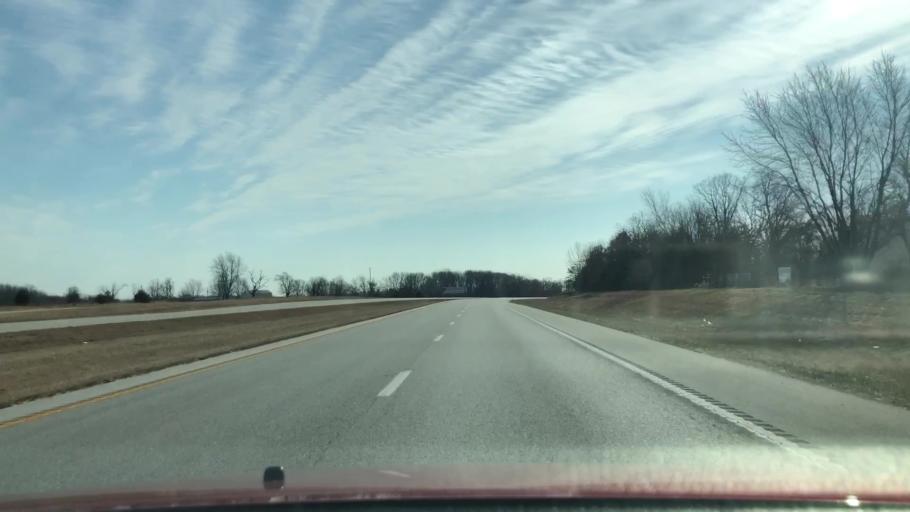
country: US
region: Missouri
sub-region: Webster County
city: Seymour
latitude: 37.1466
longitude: -92.7502
